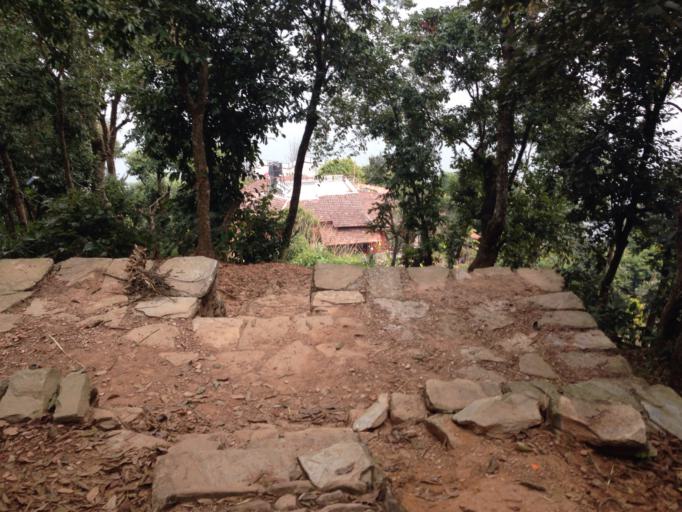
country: NP
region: Western Region
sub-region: Gandaki Zone
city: Pokhara
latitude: 28.2075
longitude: 83.9470
